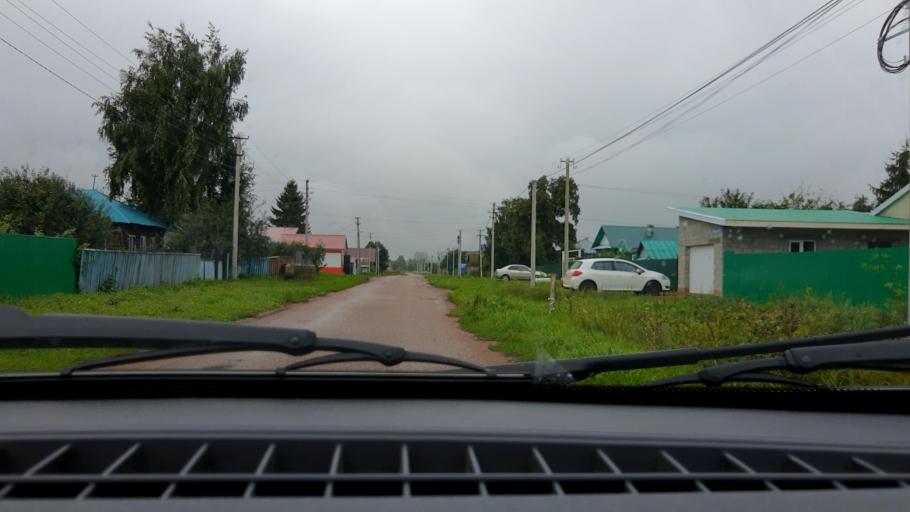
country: RU
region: Bashkortostan
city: Mikhaylovka
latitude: 54.8904
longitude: 55.8972
